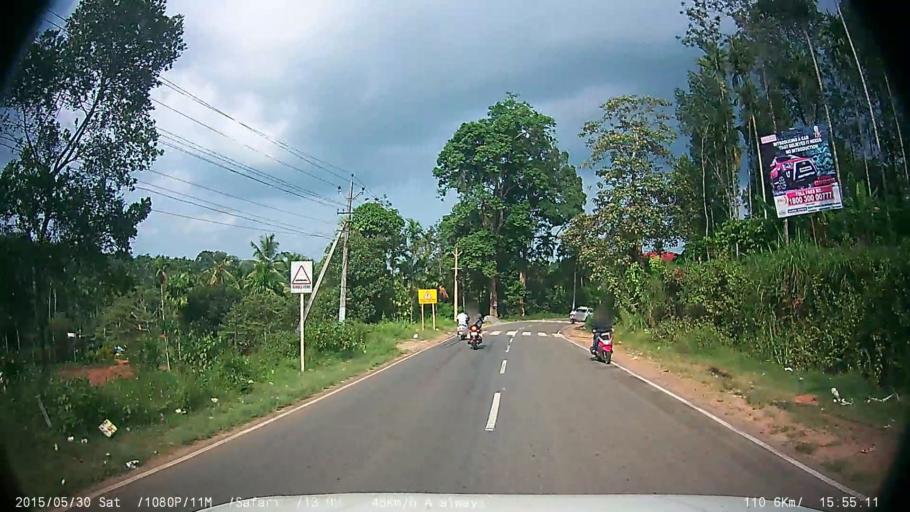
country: IN
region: Kerala
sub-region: Wayanad
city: Kalpetta
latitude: 11.6662
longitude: 76.0826
